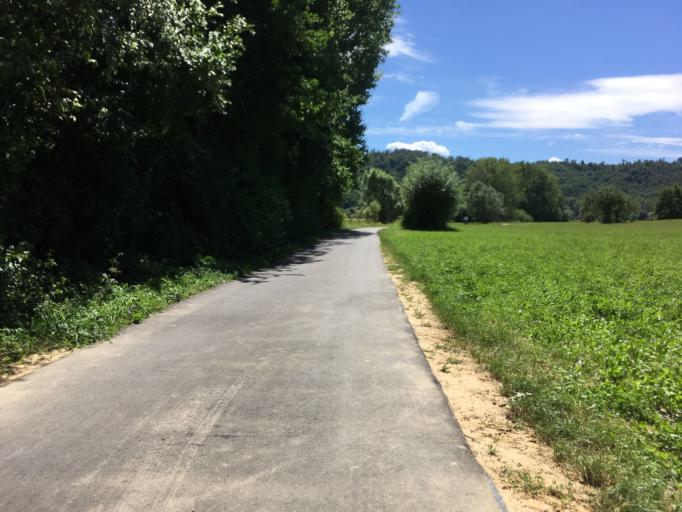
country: DE
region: Baden-Wuerttemberg
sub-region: Karlsruhe Region
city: Illingen
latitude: 48.9329
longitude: 8.9170
